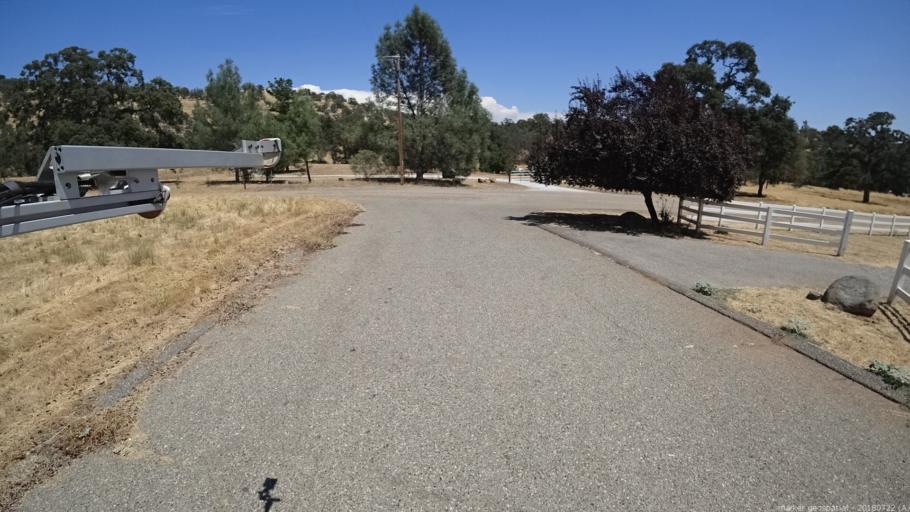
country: US
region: California
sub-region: Madera County
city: Yosemite Lakes
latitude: 37.2322
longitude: -119.7496
